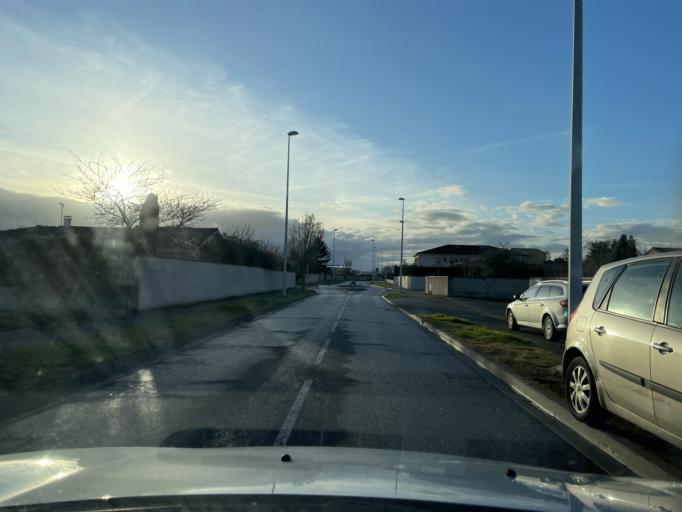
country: FR
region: Midi-Pyrenees
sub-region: Departement de la Haute-Garonne
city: Tournefeuille
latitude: 43.5981
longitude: 1.3198
